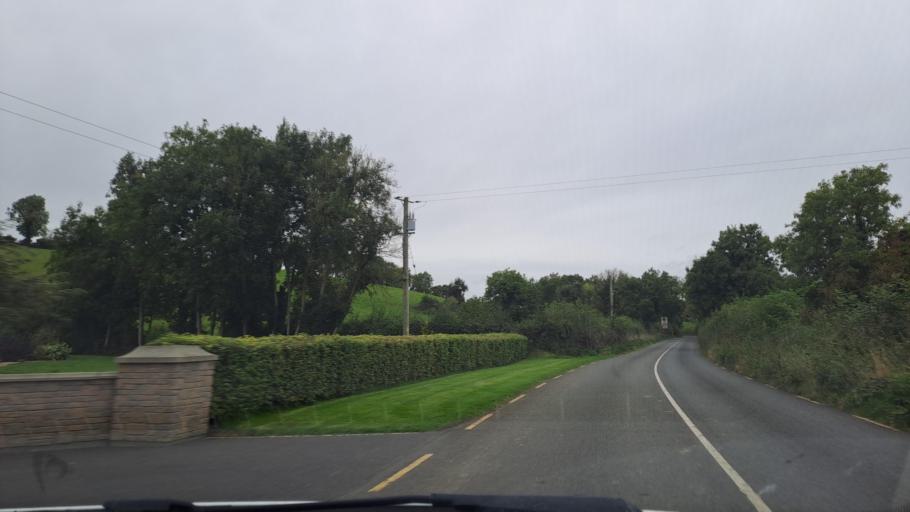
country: IE
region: Ulster
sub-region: County Monaghan
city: Carrickmacross
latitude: 53.9493
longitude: -6.6790
